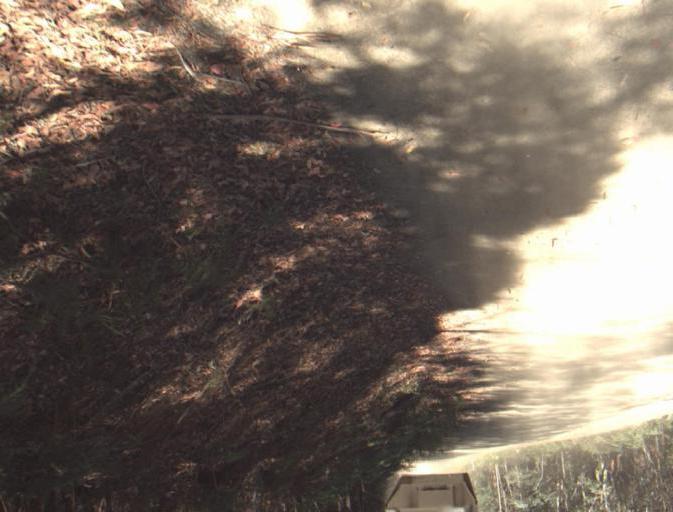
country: AU
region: Tasmania
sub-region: Dorset
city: Scottsdale
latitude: -41.3807
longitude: 147.4949
